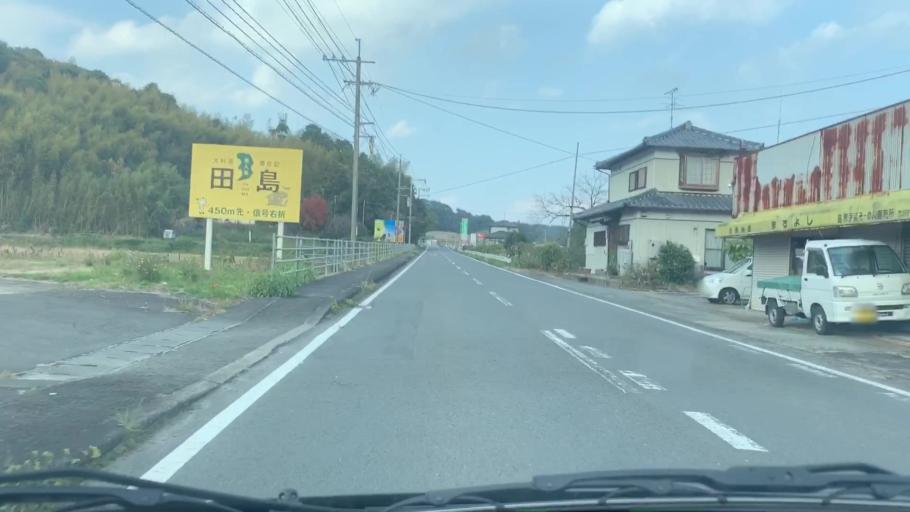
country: JP
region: Nagasaki
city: Togitsu
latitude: 32.9655
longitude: 129.7807
